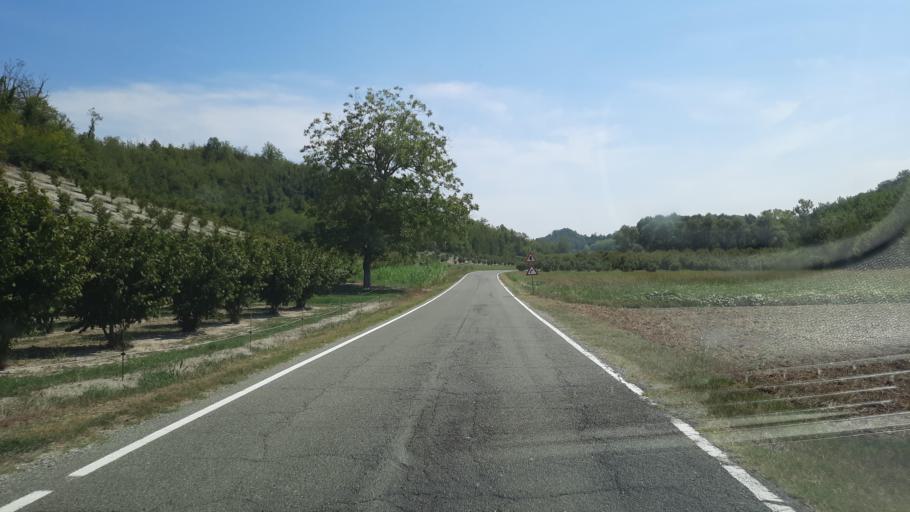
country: IT
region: Piedmont
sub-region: Provincia di Alessandria
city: Camino
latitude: 45.1518
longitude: 8.2686
